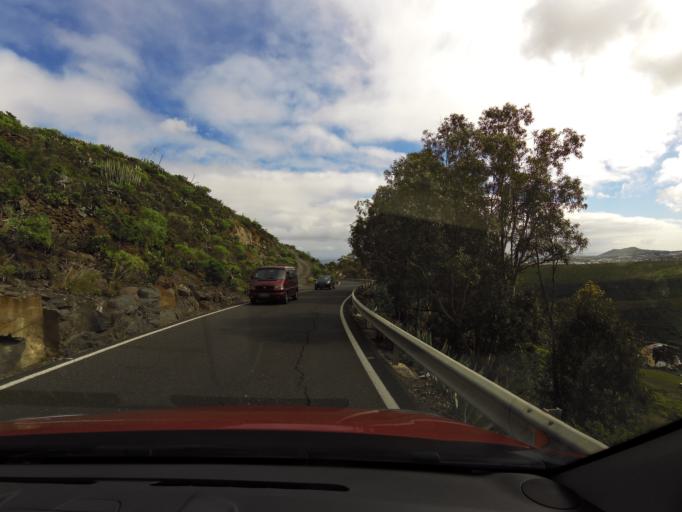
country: ES
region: Canary Islands
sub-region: Provincia de Las Palmas
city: Telde
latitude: 28.0136
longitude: -15.4402
